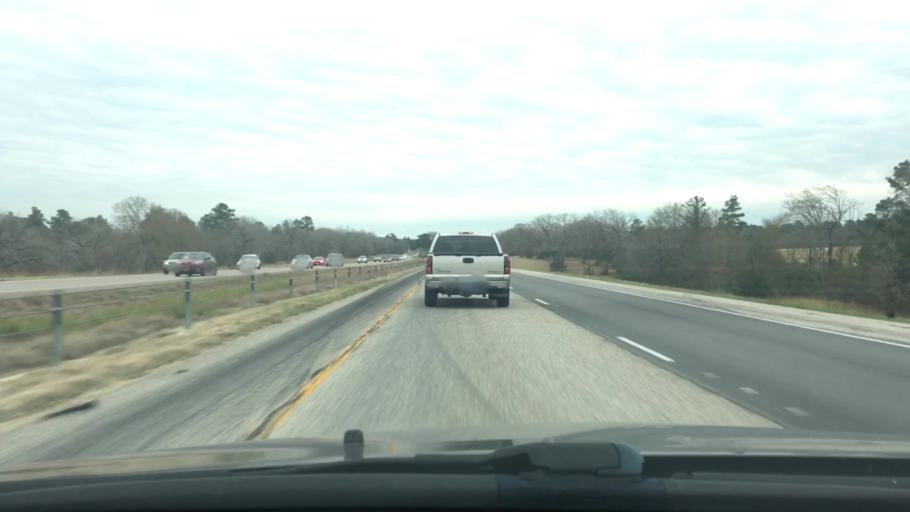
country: US
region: Texas
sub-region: Walker County
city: Huntsville
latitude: 30.7706
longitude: -95.6413
